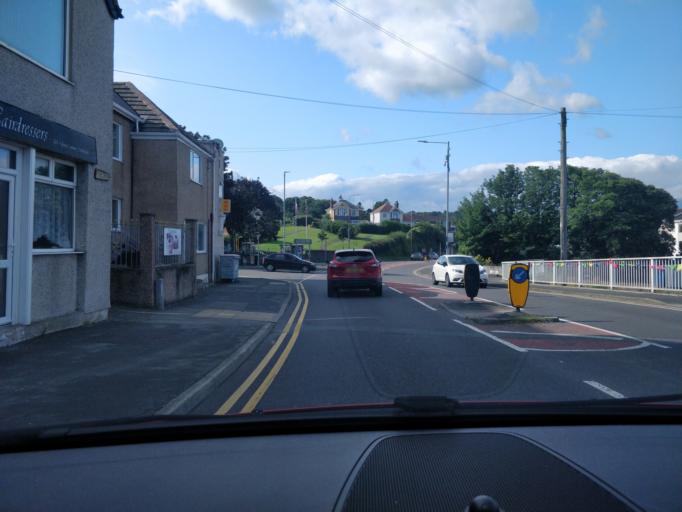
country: GB
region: Wales
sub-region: Conwy
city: Llansantffraid Glan Conwy
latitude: 53.2686
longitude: -3.7965
